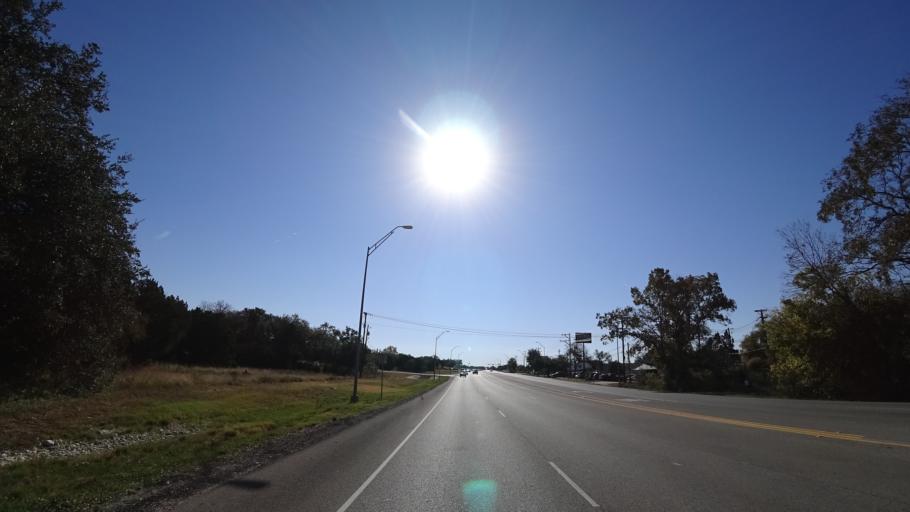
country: US
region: Texas
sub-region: Williamson County
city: Cedar Park
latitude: 30.4884
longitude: -97.8082
